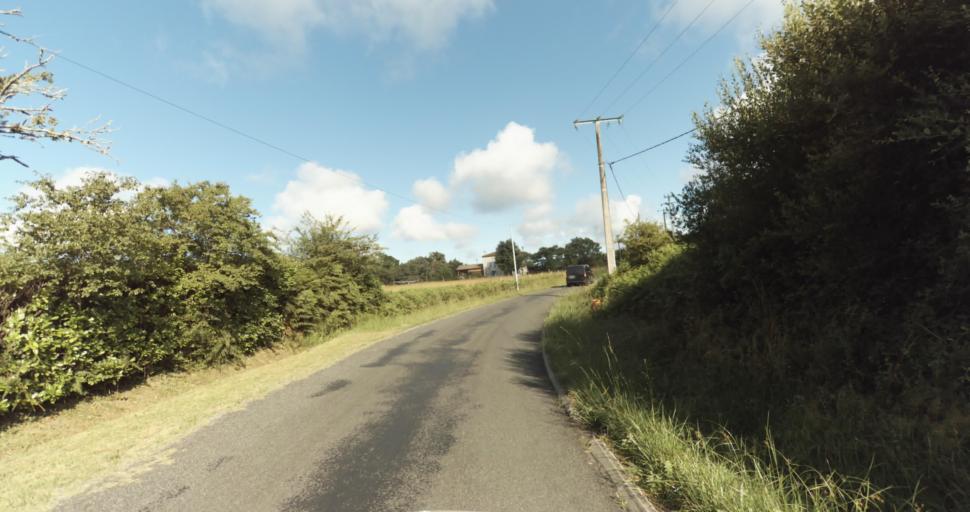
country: FR
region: Aquitaine
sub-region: Departement de la Gironde
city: Bazas
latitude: 44.4317
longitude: -0.2463
